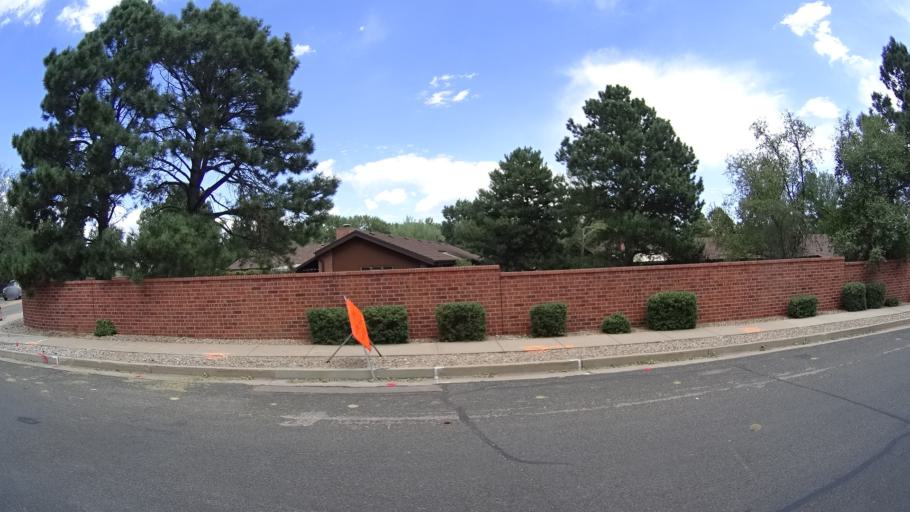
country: US
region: Colorado
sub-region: El Paso County
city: Colorado Springs
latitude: 38.7915
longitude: -104.8272
